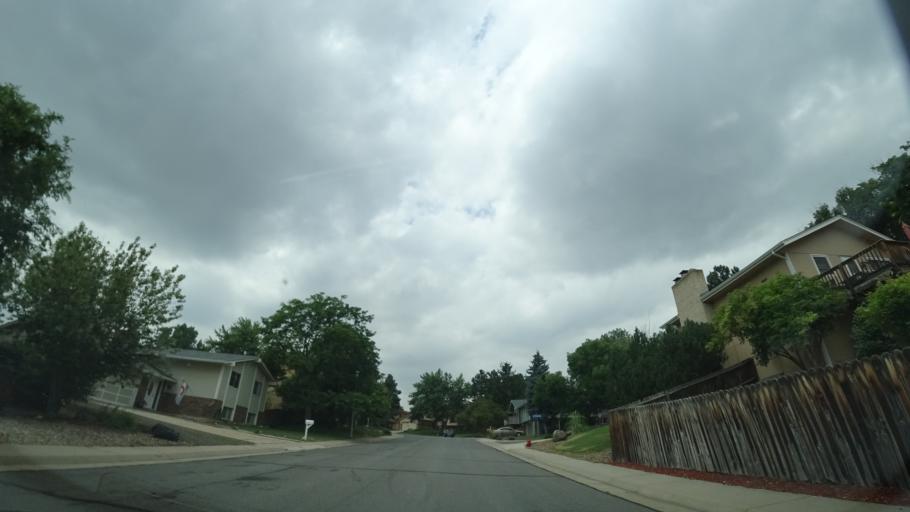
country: US
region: Colorado
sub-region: Jefferson County
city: West Pleasant View
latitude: 39.7166
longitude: -105.1452
